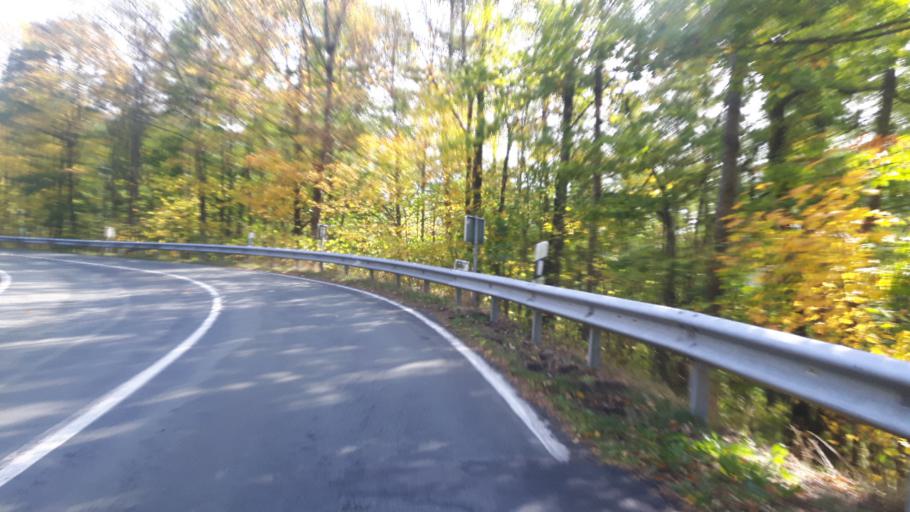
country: DE
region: North Rhine-Westphalia
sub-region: Regierungsbezirk Arnsberg
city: Erndtebruck
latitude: 50.9133
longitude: 8.2129
